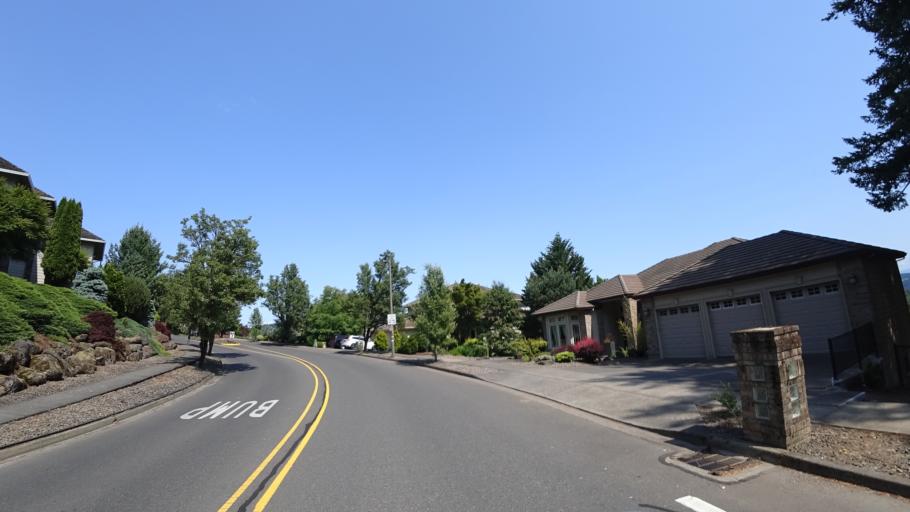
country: US
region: Oregon
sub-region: Clackamas County
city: Happy Valley
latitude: 45.4397
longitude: -122.5433
